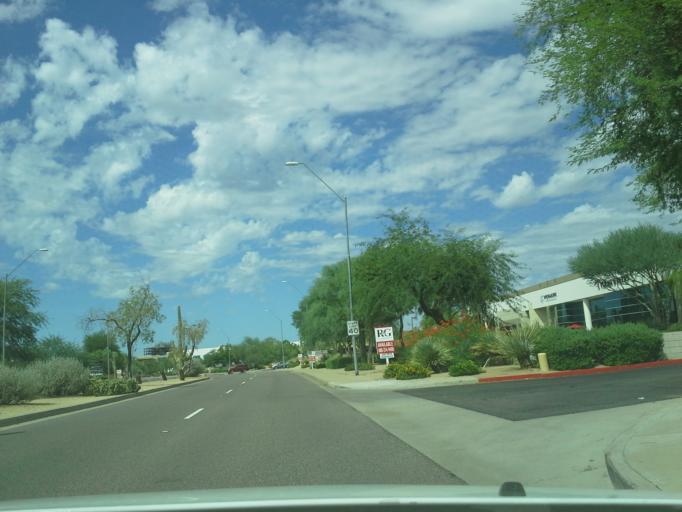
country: US
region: Arizona
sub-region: Maricopa County
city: Paradise Valley
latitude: 33.6276
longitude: -111.9178
